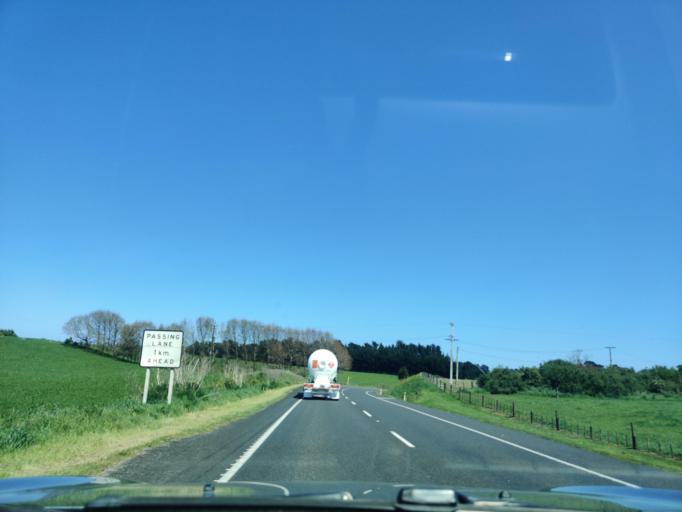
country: NZ
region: Manawatu-Wanganui
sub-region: Wanganui District
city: Wanganui
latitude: -39.8234
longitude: 174.8493
